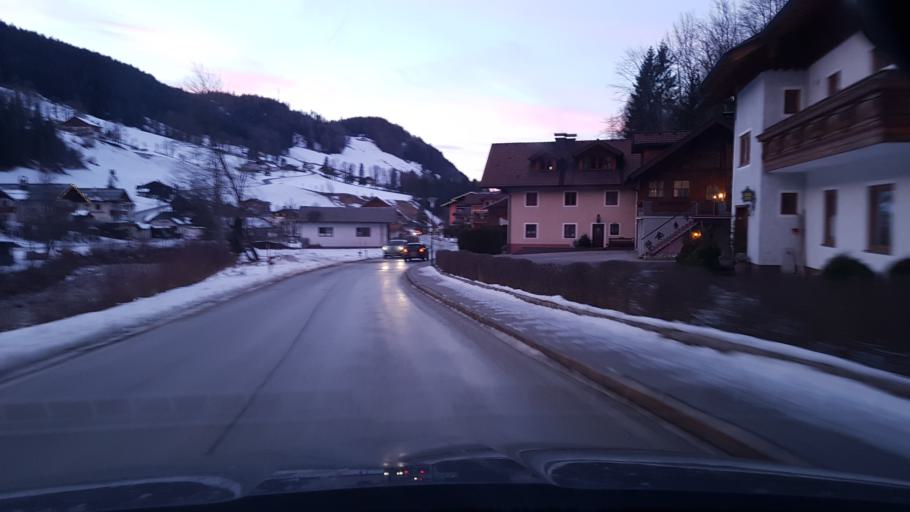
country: AT
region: Salzburg
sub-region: Politischer Bezirk Hallein
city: Krispl
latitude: 47.7097
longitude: 13.1978
